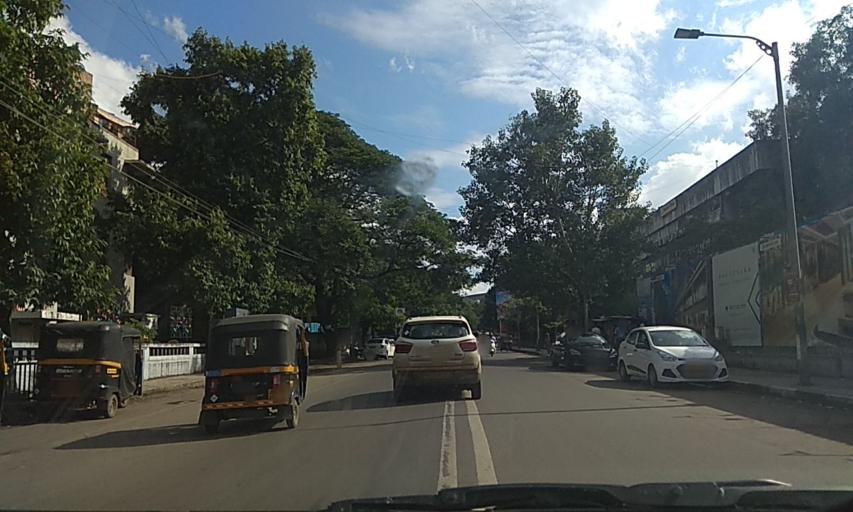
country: IN
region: Maharashtra
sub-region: Pune Division
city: Pune
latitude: 18.5264
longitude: 73.8766
